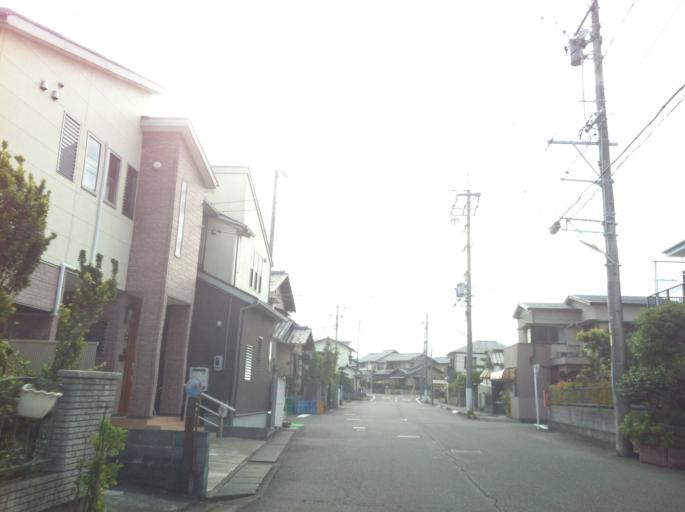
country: JP
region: Shizuoka
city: Shizuoka-shi
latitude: 35.0023
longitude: 138.4816
